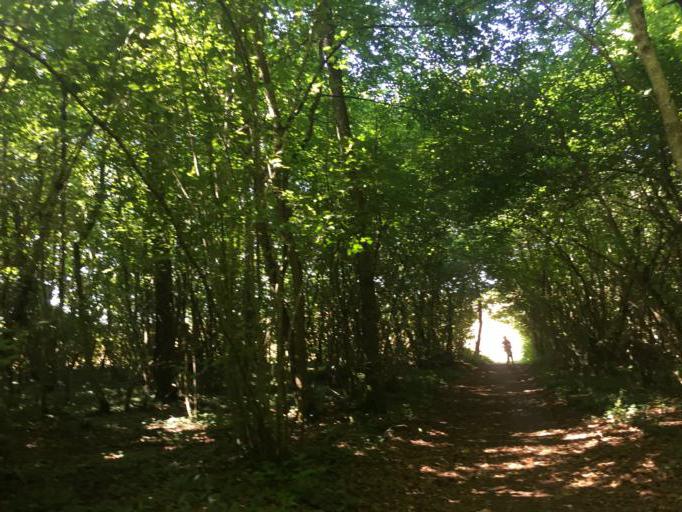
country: FR
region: Bourgogne
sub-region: Departement de l'Yonne
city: Fontenailles
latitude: 47.5918
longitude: 3.3373
